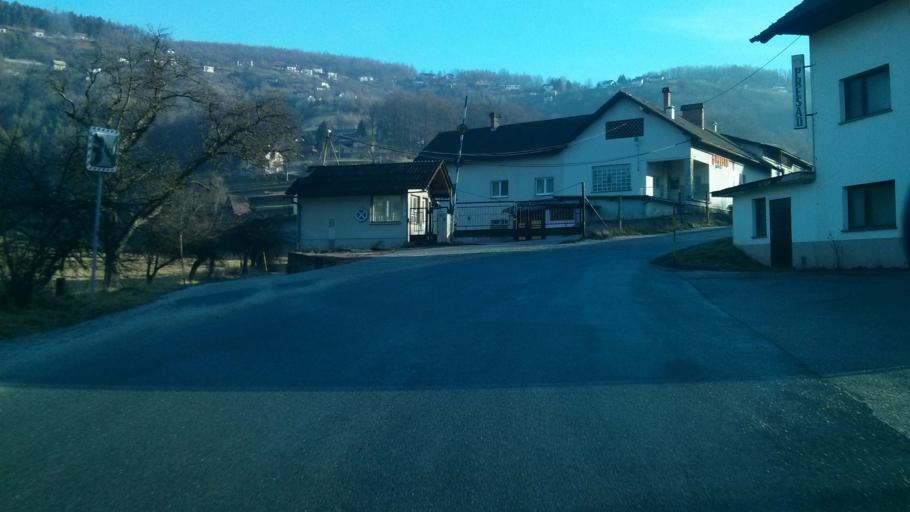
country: SI
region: Trebnje
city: Mirna
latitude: 46.0007
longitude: 14.9841
